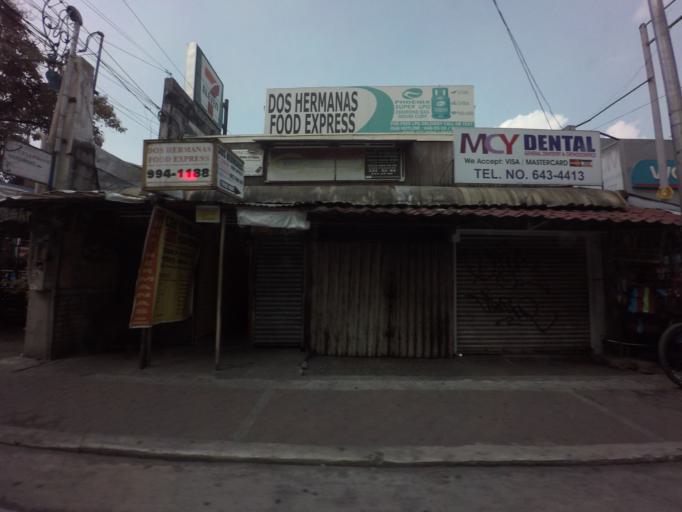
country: PH
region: Calabarzon
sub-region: Province of Rizal
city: Pateros
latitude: 14.5449
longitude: 121.0670
